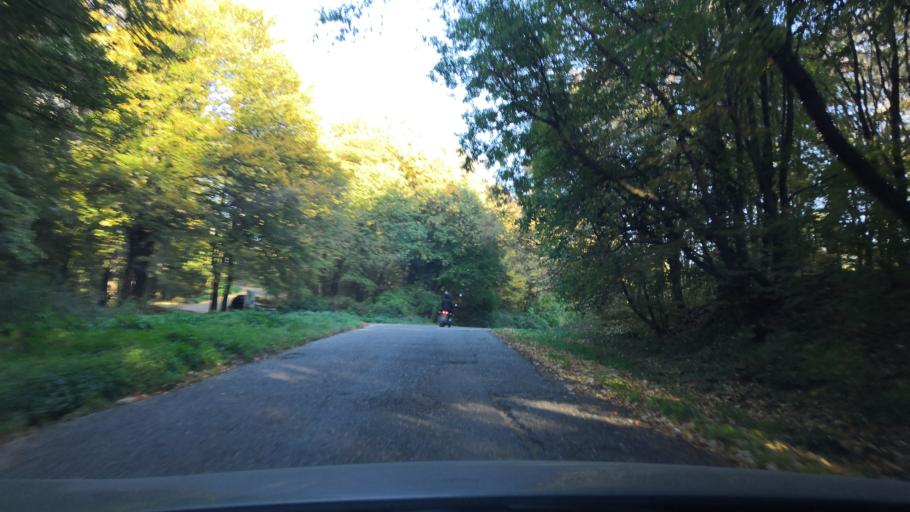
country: RS
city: Vrdnik
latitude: 45.1562
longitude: 19.8079
